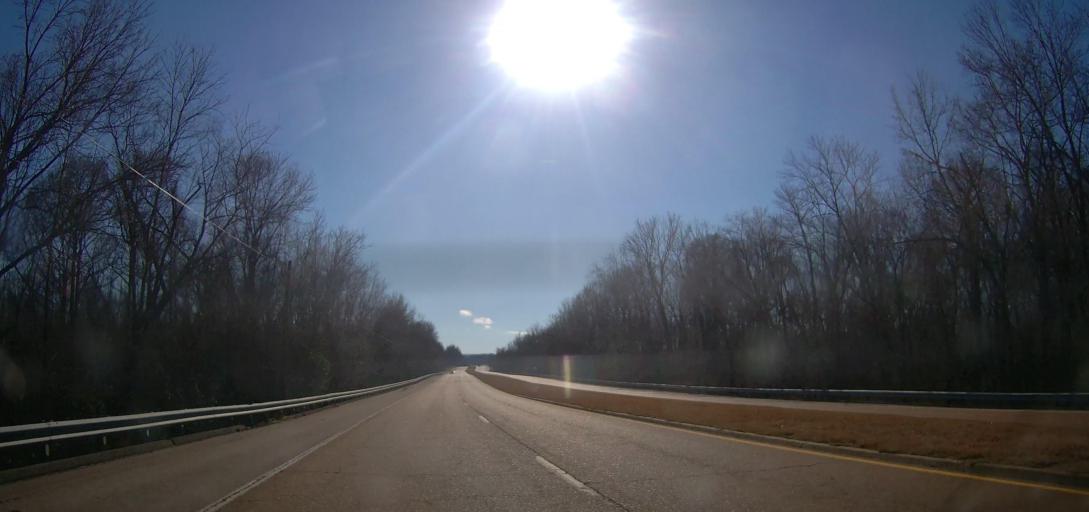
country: US
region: Tennessee
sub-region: Shelby County
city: Millington
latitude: 35.2730
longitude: -89.8875
